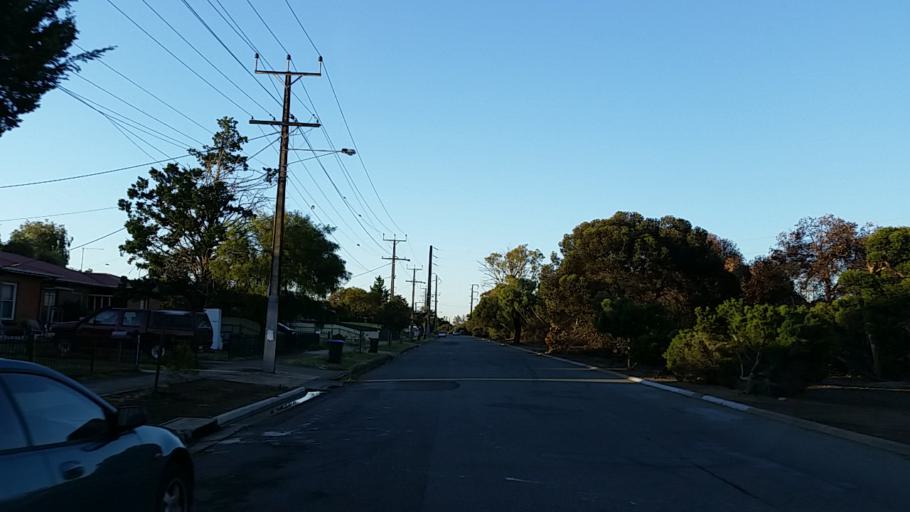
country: AU
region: South Australia
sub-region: Port Adelaide Enfield
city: Birkenhead
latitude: -34.8077
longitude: 138.5066
